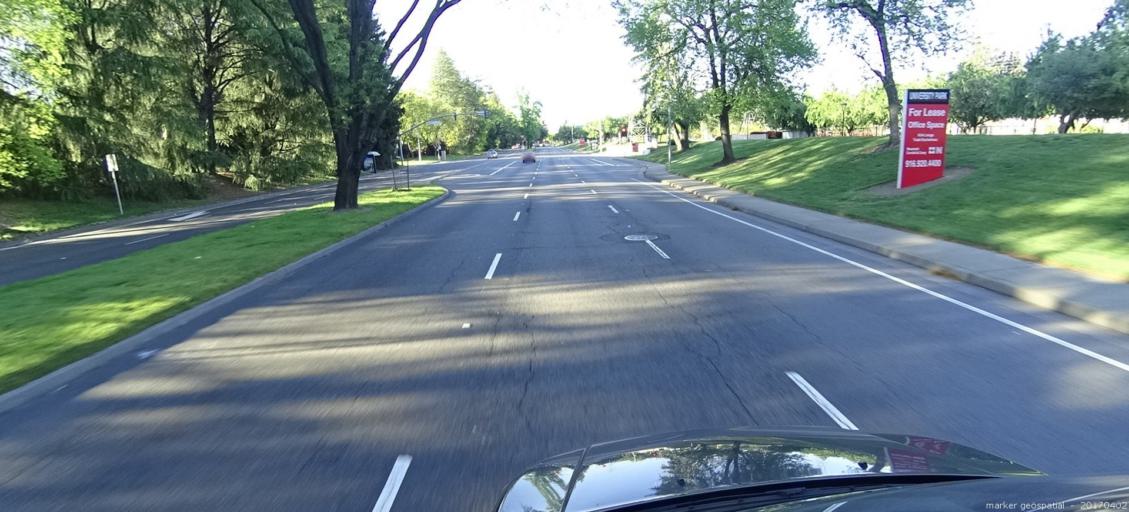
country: US
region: California
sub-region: Sacramento County
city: Rosemont
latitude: 38.5643
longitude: -121.4090
